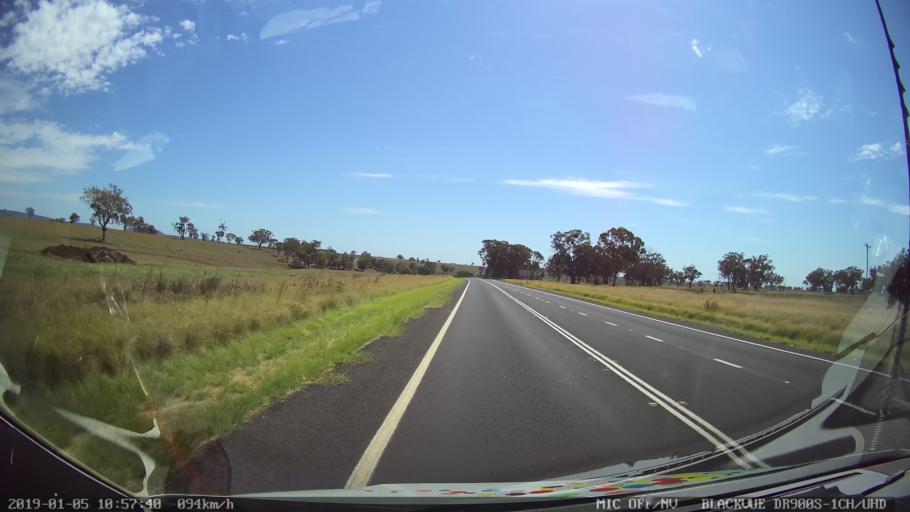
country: AU
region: New South Wales
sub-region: Warrumbungle Shire
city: Coonabarabran
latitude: -31.4293
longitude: 149.1728
